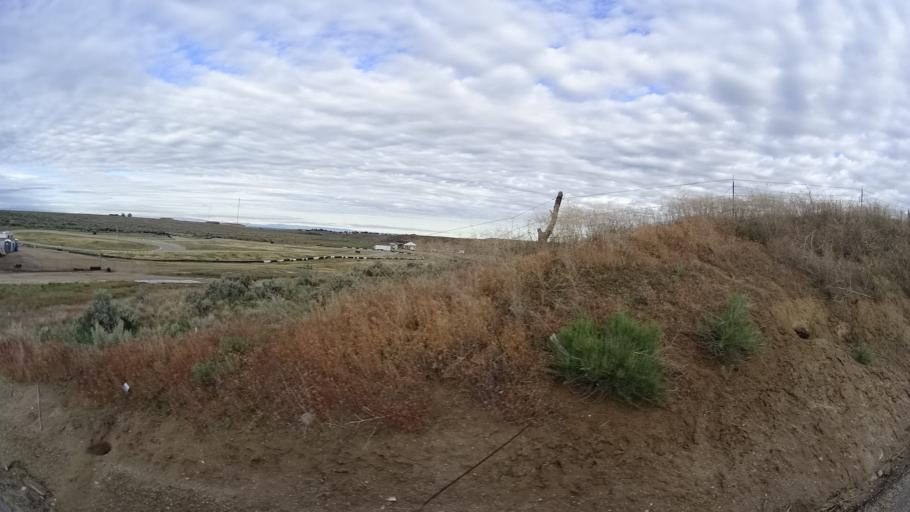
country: US
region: Idaho
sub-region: Ada County
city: Star
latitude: 43.7300
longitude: -116.5127
